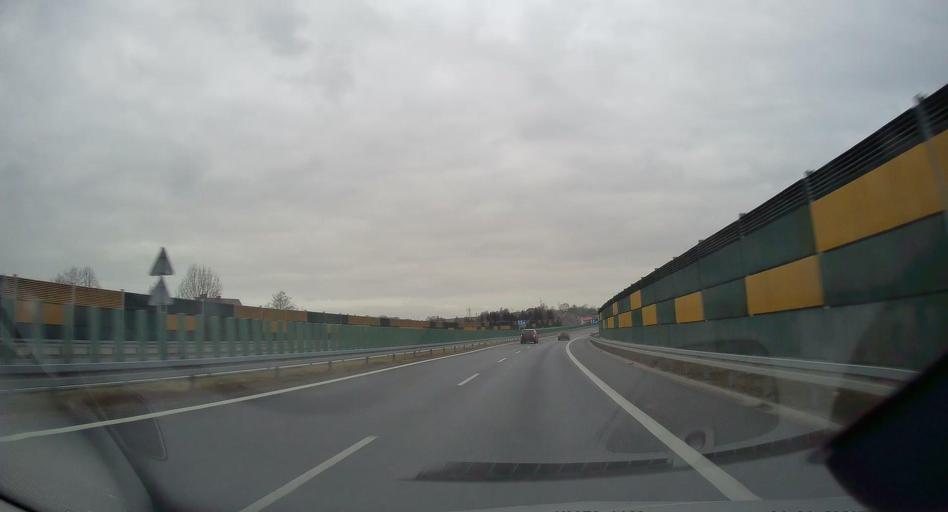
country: PL
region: Subcarpathian Voivodeship
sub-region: Powiat ropczycko-sedziszowski
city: Ropczyce
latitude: 50.0510
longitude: 21.6017
